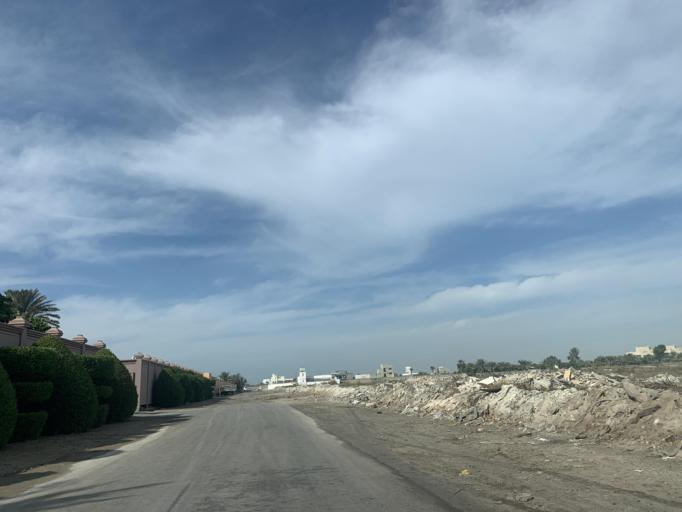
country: BH
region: Central Governorate
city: Madinat Hamad
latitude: 26.1203
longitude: 50.4658
